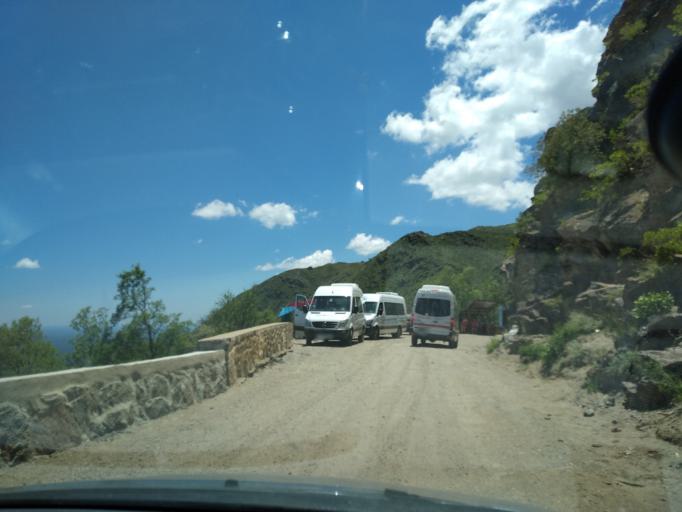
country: AR
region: Cordoba
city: Salsacate
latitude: -31.3758
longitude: -65.4081
